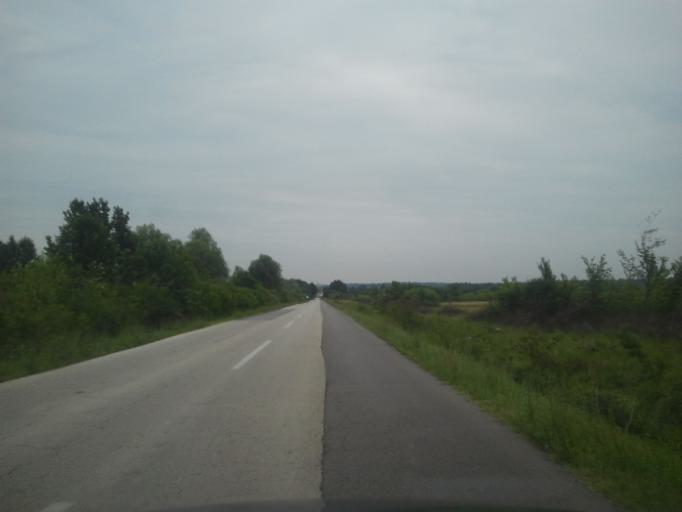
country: HR
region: Grad Zagreb
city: Horvati
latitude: 45.5570
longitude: 15.8598
